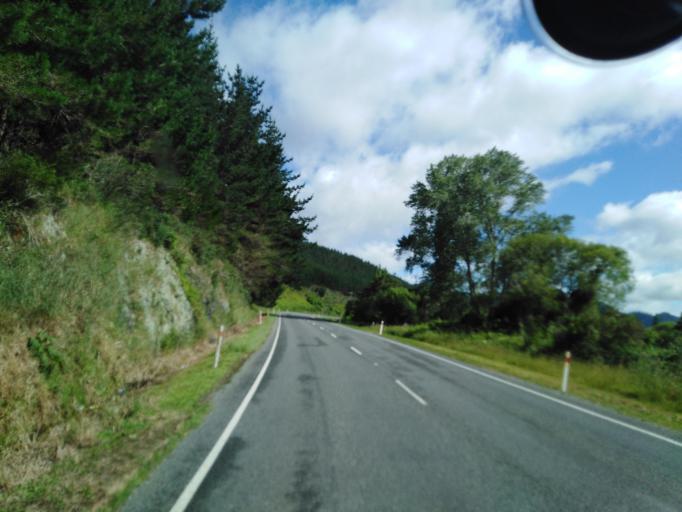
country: NZ
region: Nelson
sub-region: Nelson City
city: Nelson
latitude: -41.2478
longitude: 173.5776
